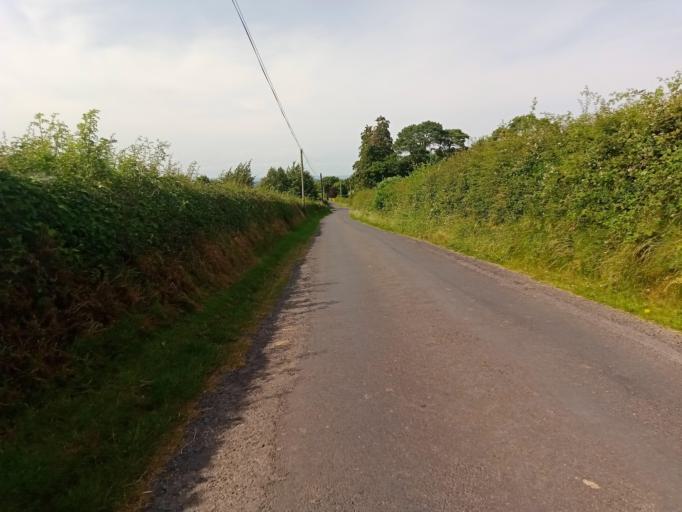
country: IE
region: Leinster
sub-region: Laois
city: Rathdowney
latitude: 52.8108
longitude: -7.4694
